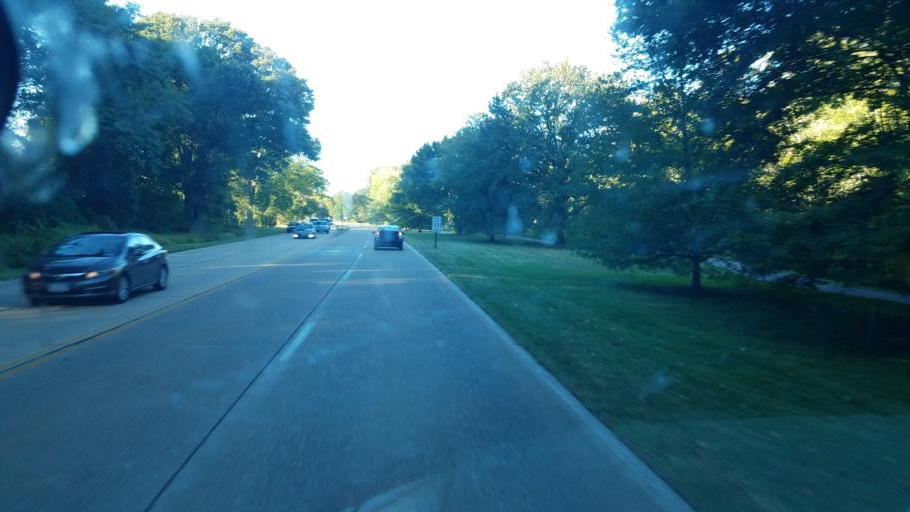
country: US
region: Virginia
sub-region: Fairfax County
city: Belle Haven
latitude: 38.7715
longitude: -77.0526
